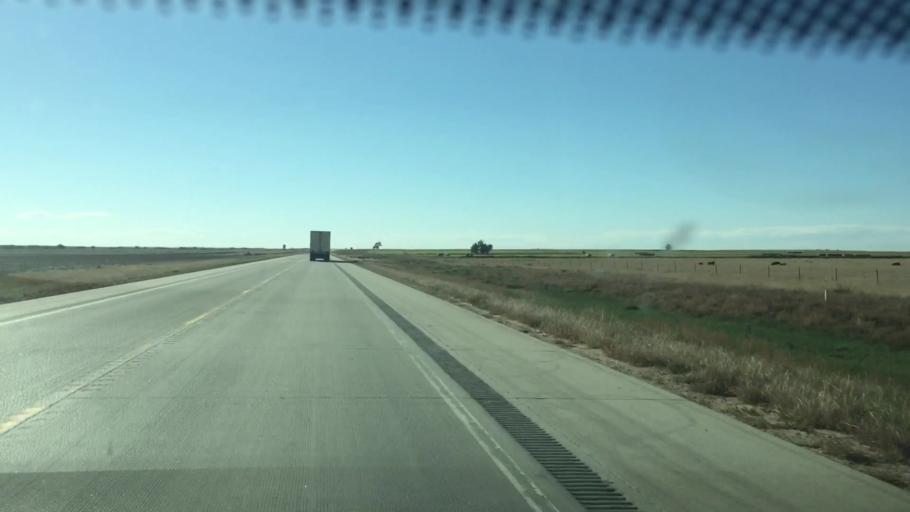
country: US
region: Colorado
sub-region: Kiowa County
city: Eads
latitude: 38.7640
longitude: -102.8104
